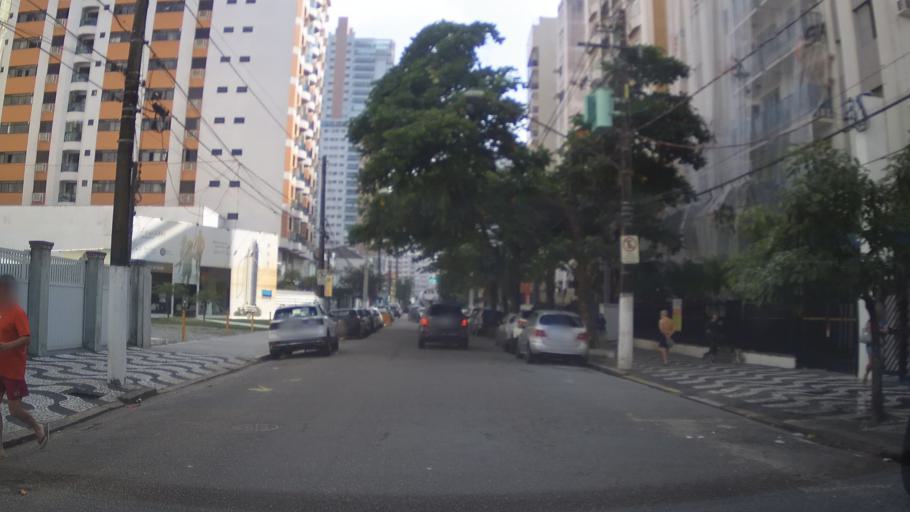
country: BR
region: Sao Paulo
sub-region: Santos
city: Santos
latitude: -23.9721
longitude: -46.3233
